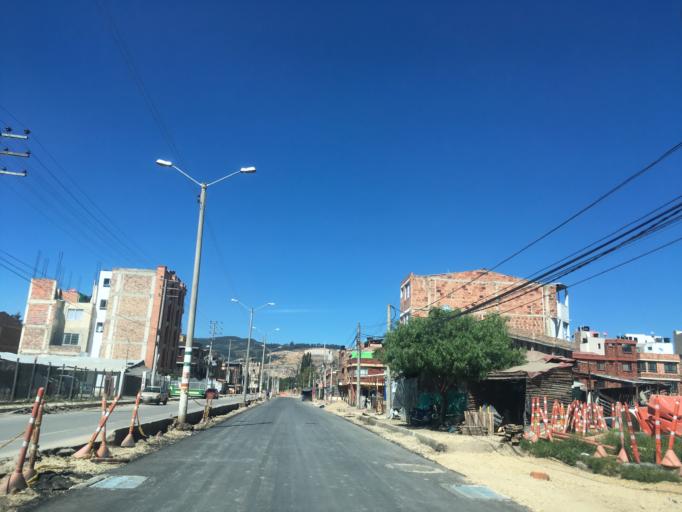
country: CO
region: Boyaca
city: Sogamoso
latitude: 5.7026
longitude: -72.9390
